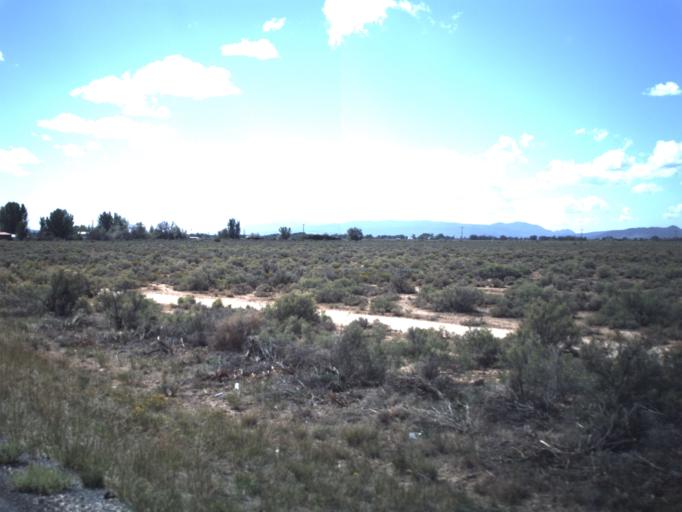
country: US
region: Utah
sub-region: Iron County
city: Enoch
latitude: 37.7902
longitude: -113.0507
